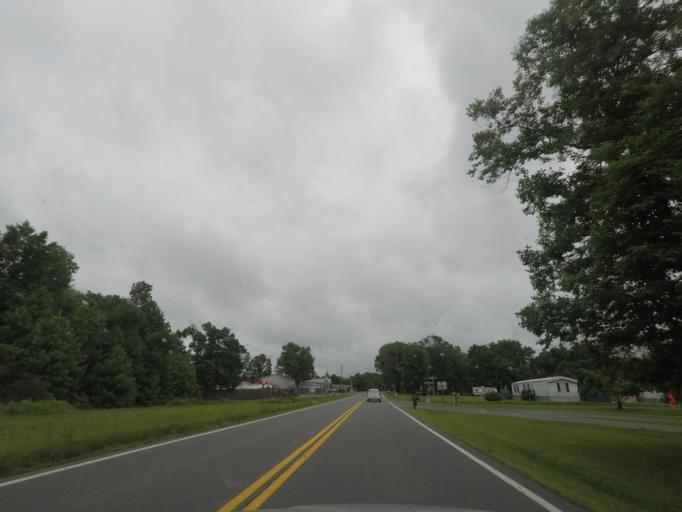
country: US
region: Virginia
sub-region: Fluvanna County
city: Palmyra
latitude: 37.9400
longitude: -78.2453
